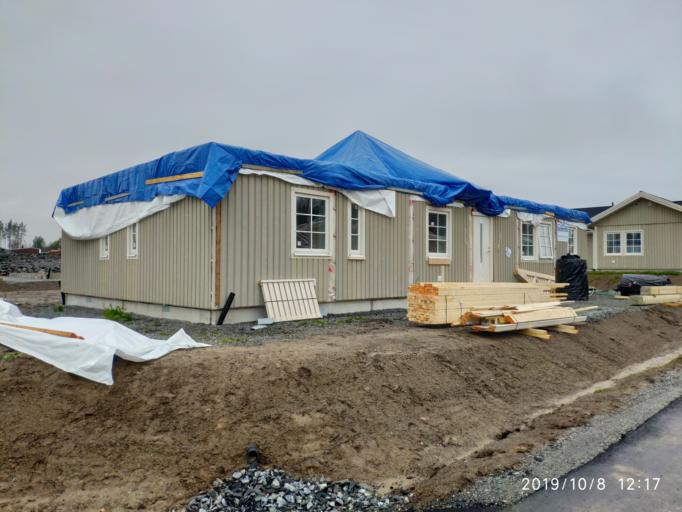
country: NO
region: Akershus
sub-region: Nes
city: Arnes
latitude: 60.1701
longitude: 11.5500
